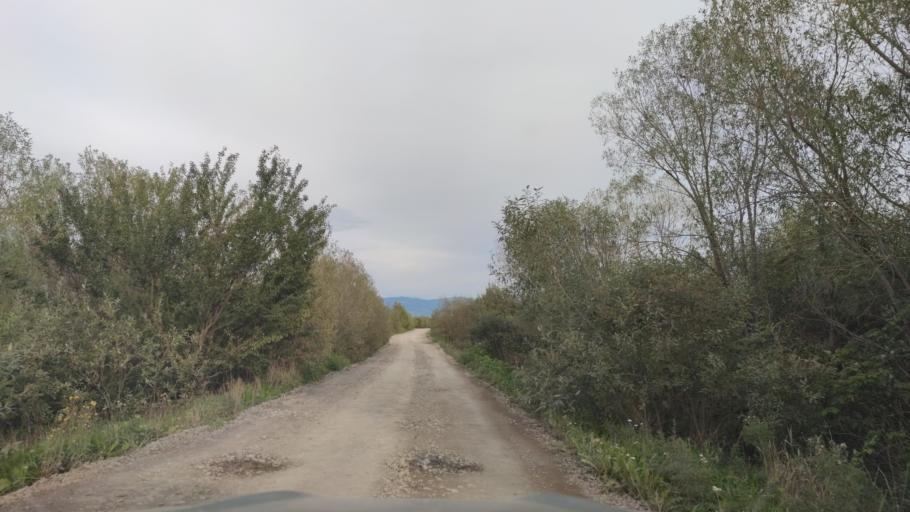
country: RO
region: Harghita
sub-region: Comuna Remetea
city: Remetea
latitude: 46.8117
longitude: 25.3831
